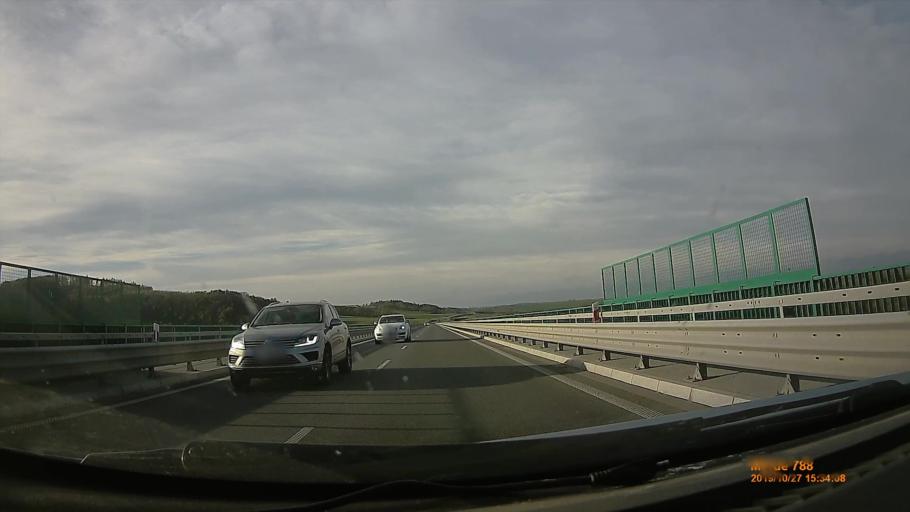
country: PL
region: Lower Silesian Voivodeship
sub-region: Powiat klodzki
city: Klodzko
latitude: 50.4027
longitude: 16.6444
